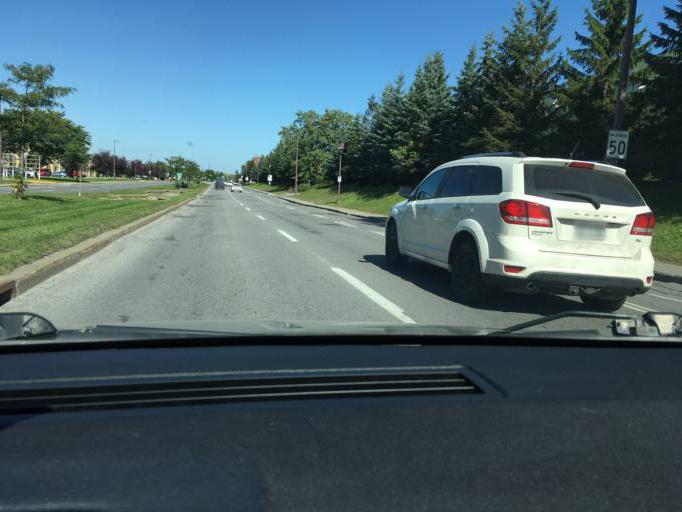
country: CA
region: Quebec
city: Dorval
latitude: 45.5074
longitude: -73.7376
